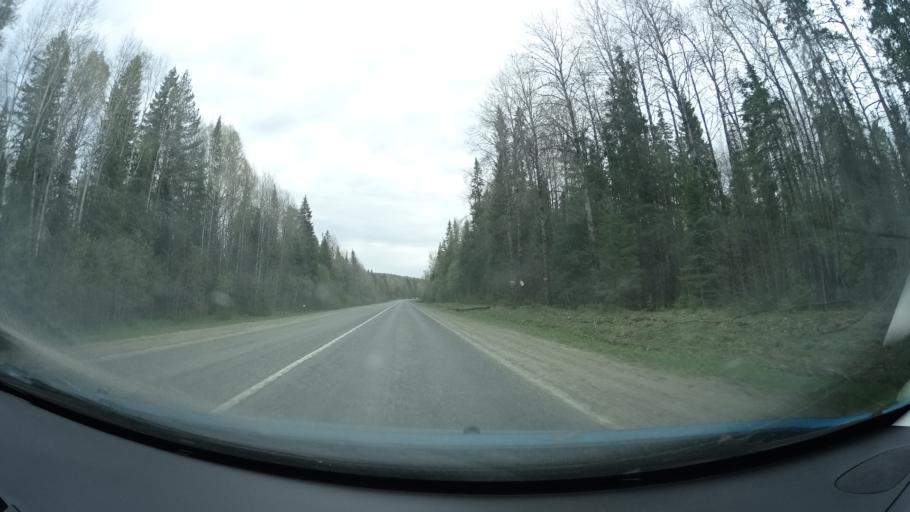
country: RU
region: Perm
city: Yugo-Kamskiy
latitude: 57.6435
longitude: 55.6041
